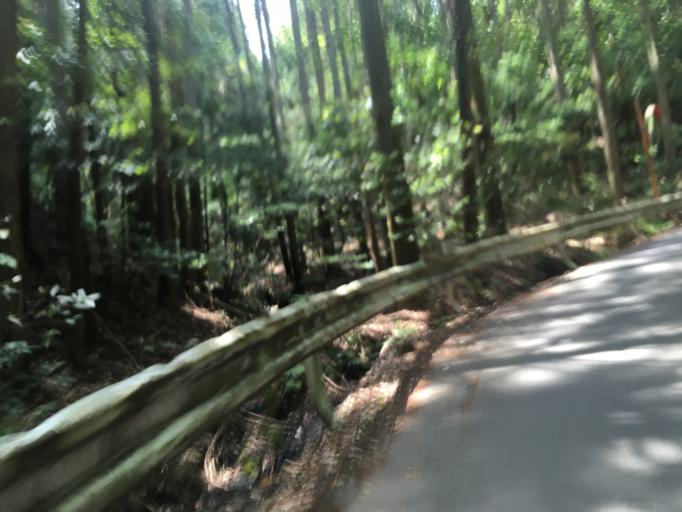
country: JP
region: Kyoto
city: Muko
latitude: 35.0291
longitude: 135.6580
